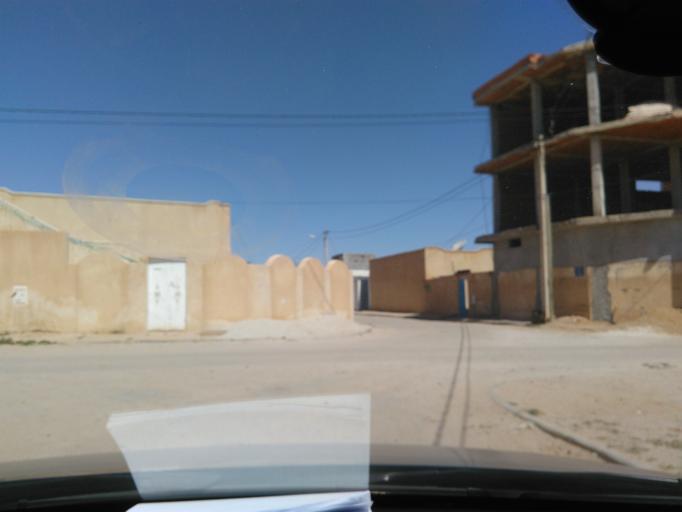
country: TN
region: Tataouine
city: Tataouine
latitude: 32.9494
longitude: 10.4678
